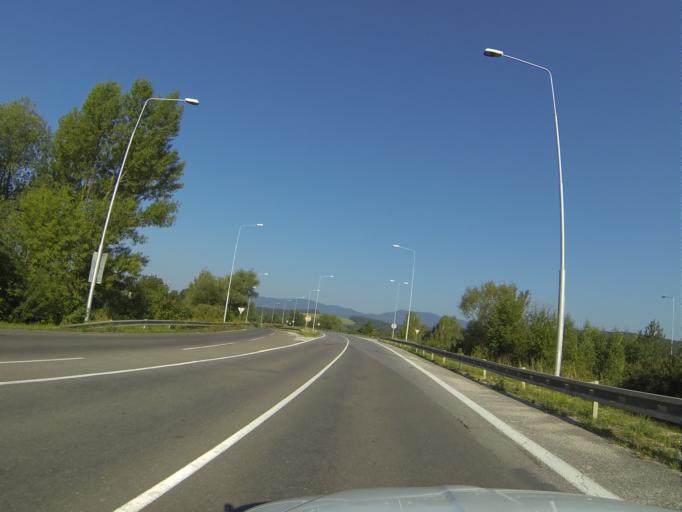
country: SK
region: Nitriansky
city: Novaky
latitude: 48.7247
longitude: 18.5529
